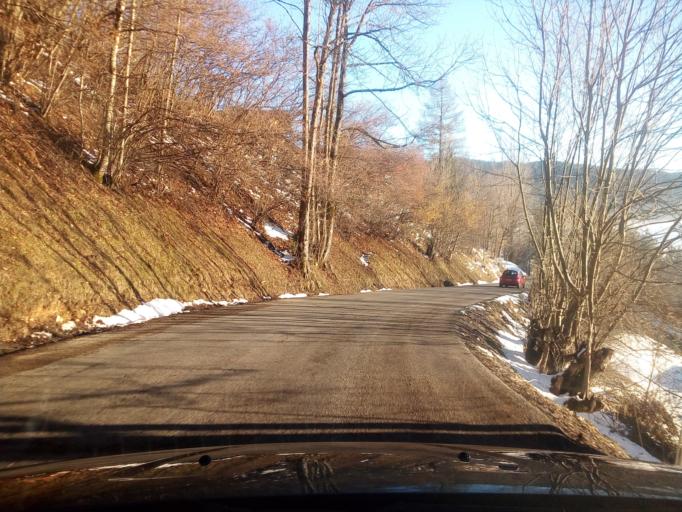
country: FR
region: Rhone-Alpes
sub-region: Departement de l'Isere
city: Le Sappey-en-Chartreuse
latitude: 45.2670
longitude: 5.7727
